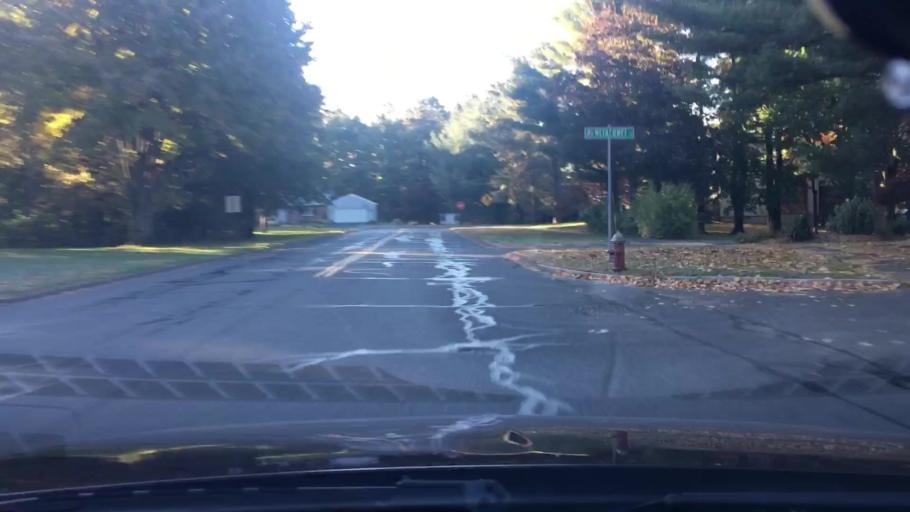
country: US
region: Connecticut
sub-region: Hartford County
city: Sherwood Manor
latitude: 42.0346
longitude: -72.5454
